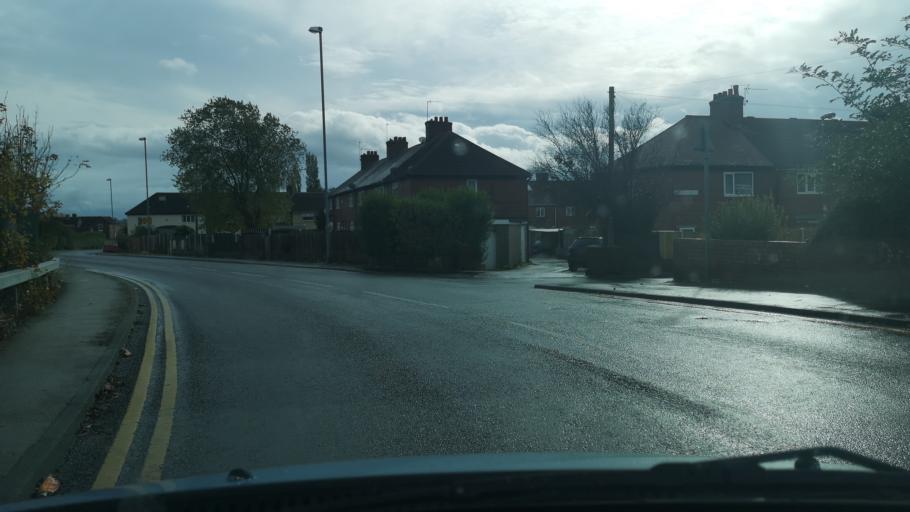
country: GB
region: England
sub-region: City and Borough of Wakefield
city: Fitzwilliam
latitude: 53.6339
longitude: -1.3775
